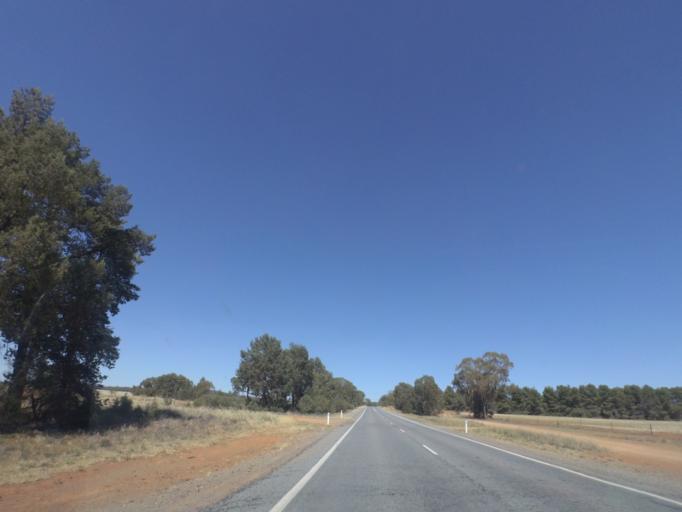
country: AU
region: New South Wales
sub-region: Narrandera
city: Narrandera
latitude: -34.4174
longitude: 146.8542
